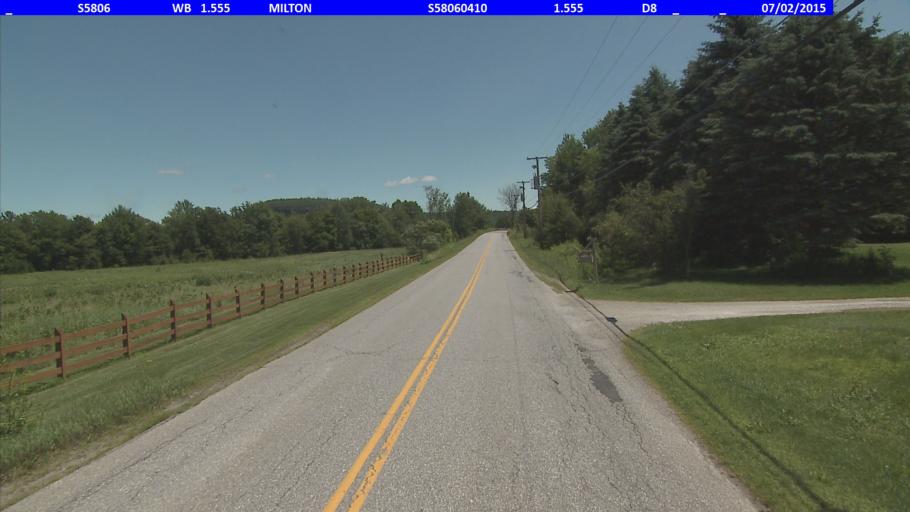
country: US
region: Vermont
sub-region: Chittenden County
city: Milton
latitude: 44.6598
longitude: -73.1415
